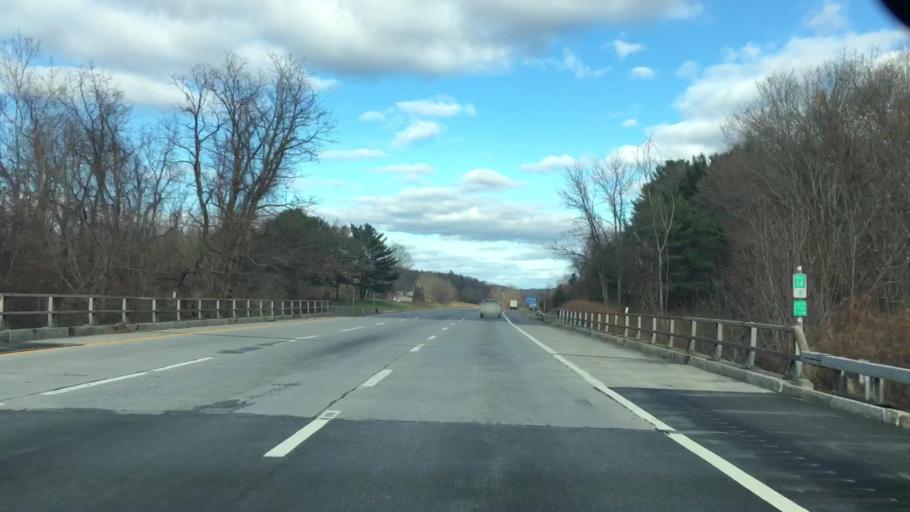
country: US
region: New York
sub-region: Westchester County
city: Bedford Hills
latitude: 41.2255
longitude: -73.6832
